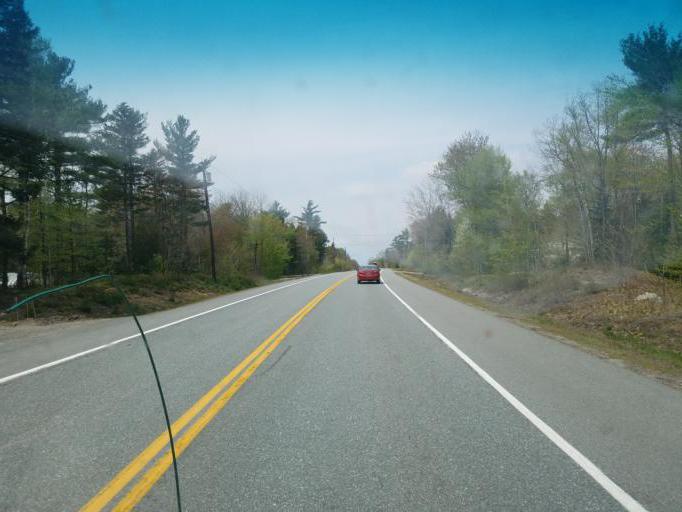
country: US
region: Maine
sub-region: Hancock County
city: Ellsworth
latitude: 44.5846
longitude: -68.4921
